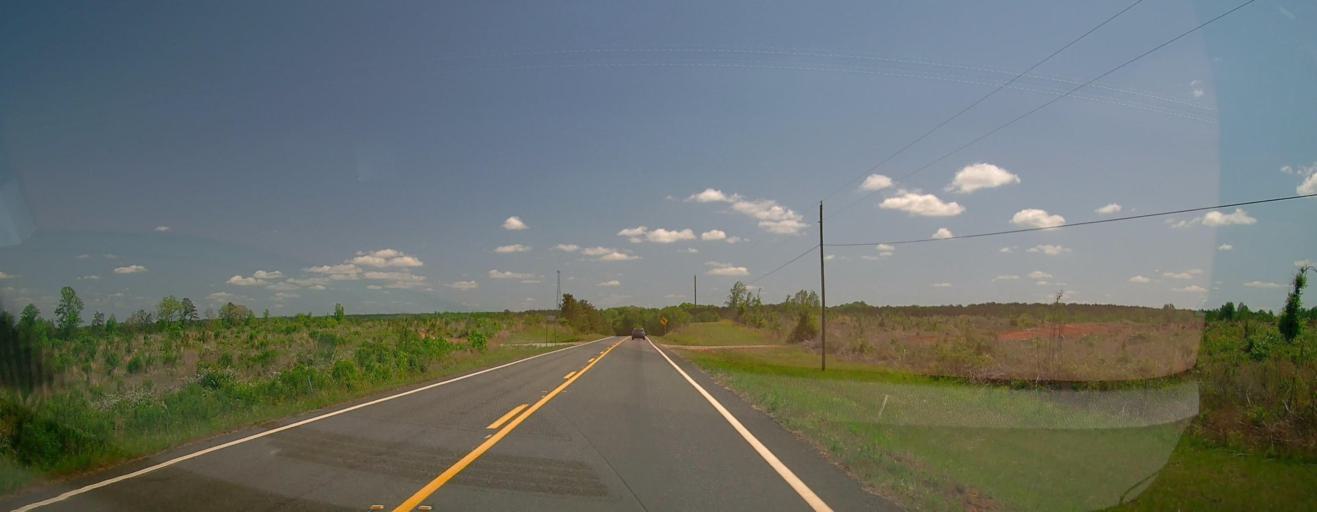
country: US
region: Georgia
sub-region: Jasper County
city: Monticello
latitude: 33.2415
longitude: -83.5535
